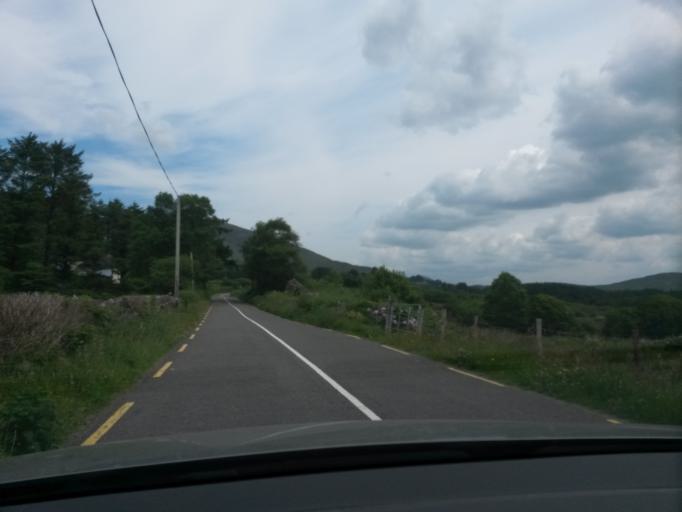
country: IE
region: Munster
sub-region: Ciarrai
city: Kenmare
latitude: 51.9093
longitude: -9.7223
